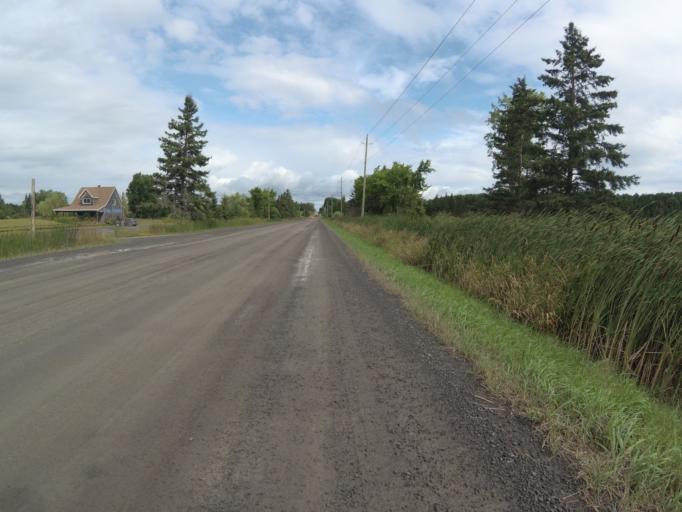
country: CA
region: Ontario
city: Clarence-Rockland
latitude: 45.4819
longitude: -75.3097
